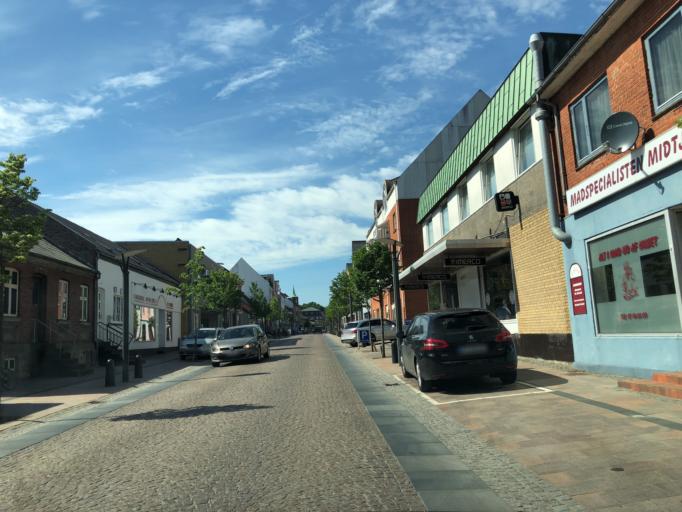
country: DK
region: Central Jutland
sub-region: Ikast-Brande Kommune
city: Brande
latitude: 55.9421
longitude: 9.1293
